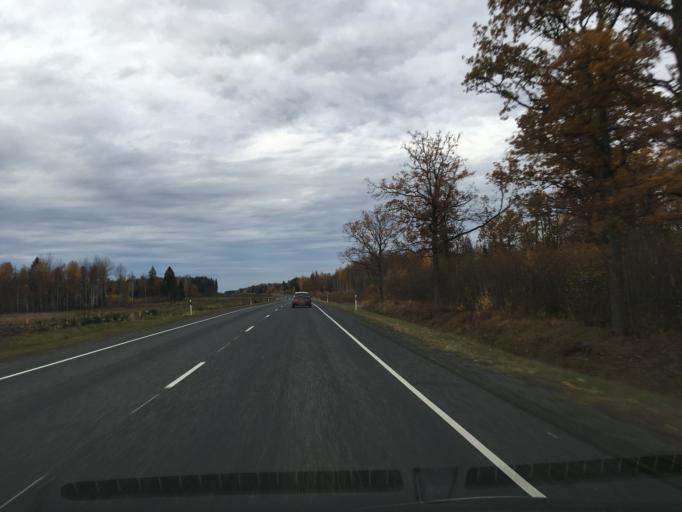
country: EE
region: Harju
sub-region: Nissi vald
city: Turba
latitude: 58.9455
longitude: 24.0854
